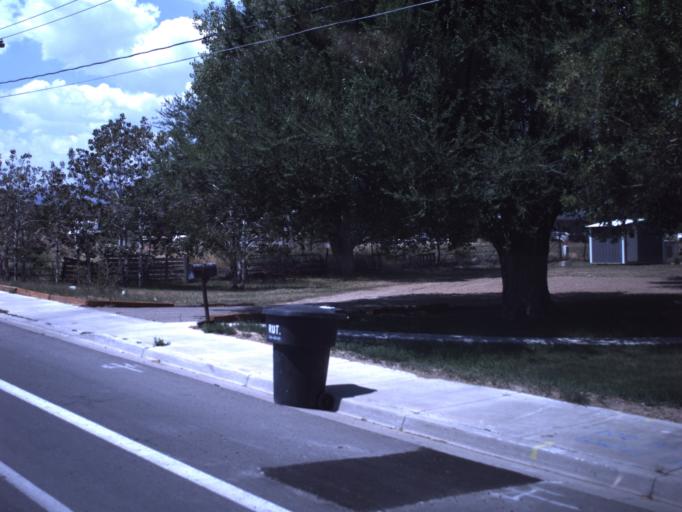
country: US
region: Utah
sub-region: Uintah County
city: Maeser
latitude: 40.4627
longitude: -109.5600
